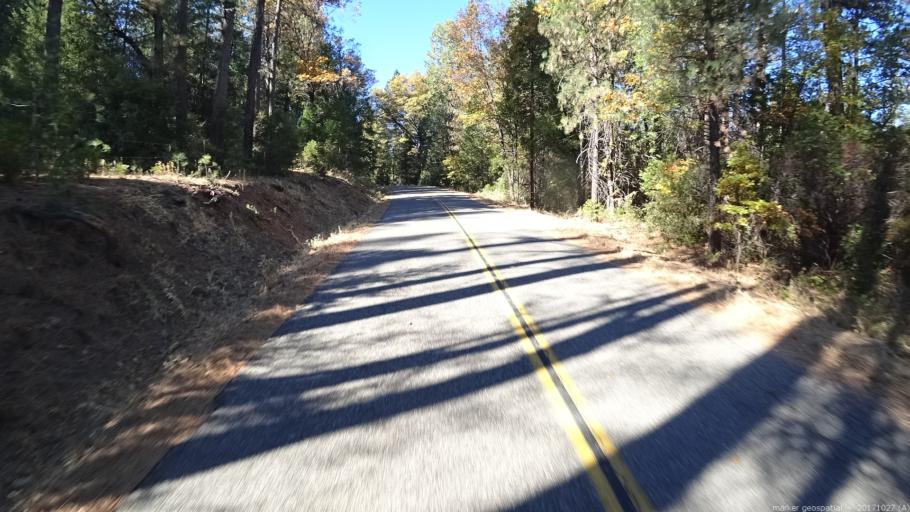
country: US
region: California
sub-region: Shasta County
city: Shingletown
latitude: 40.6861
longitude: -121.9066
